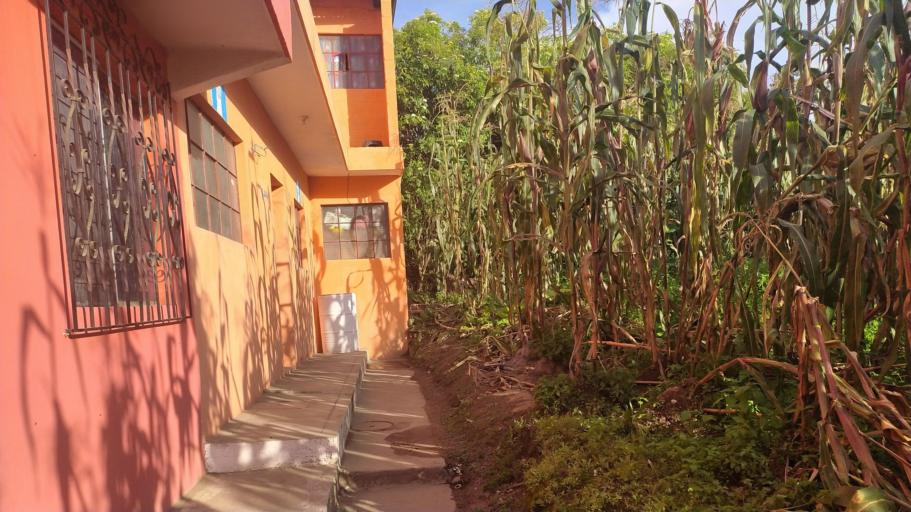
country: GT
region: Quetzaltenango
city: Salcaja
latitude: 14.8706
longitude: -91.4595
